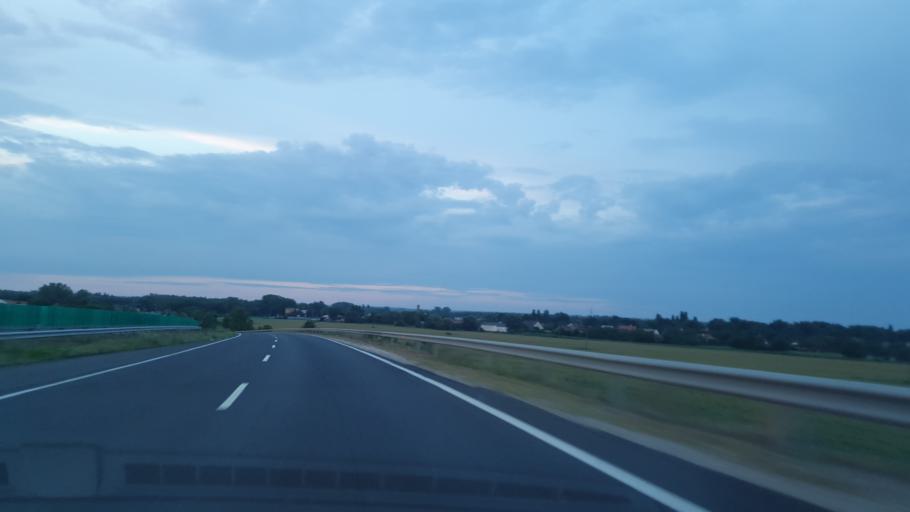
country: HU
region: Fejer
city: Szekesfehervar
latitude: 47.1970
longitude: 18.3846
